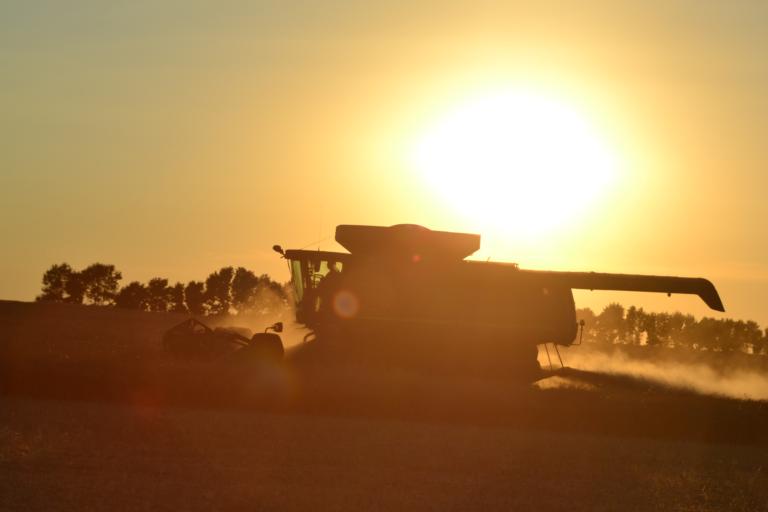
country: US
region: North Dakota
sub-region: Mercer County
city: Beulah
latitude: 47.6870
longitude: -101.9021
